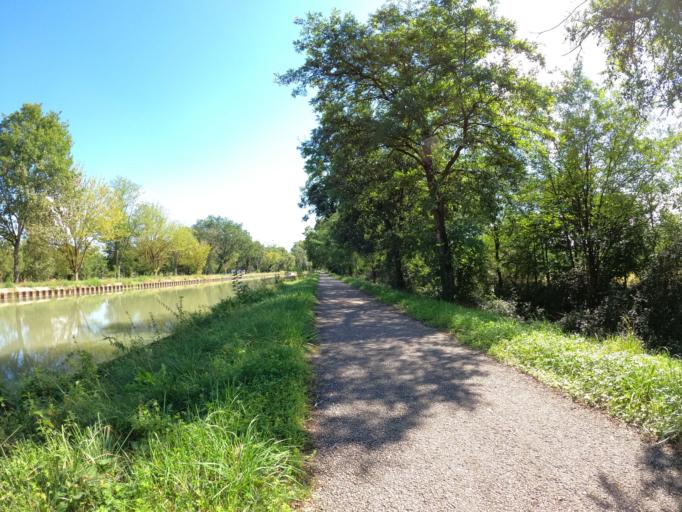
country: FR
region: Midi-Pyrenees
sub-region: Departement du Tarn-et-Garonne
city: Lamagistere
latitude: 44.1257
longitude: 0.8396
